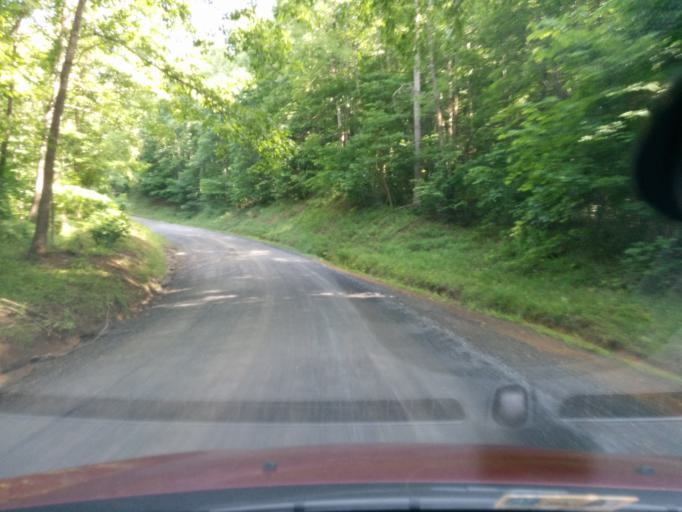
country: US
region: Virginia
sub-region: City of Lexington
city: Lexington
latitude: 37.7834
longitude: -79.5013
